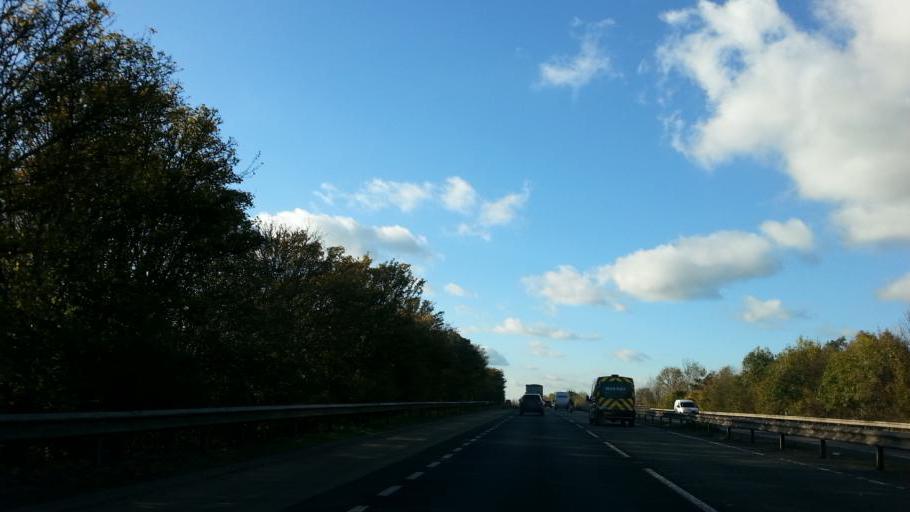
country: GB
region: England
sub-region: Suffolk
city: Newmarket
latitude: 52.2711
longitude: 0.5243
